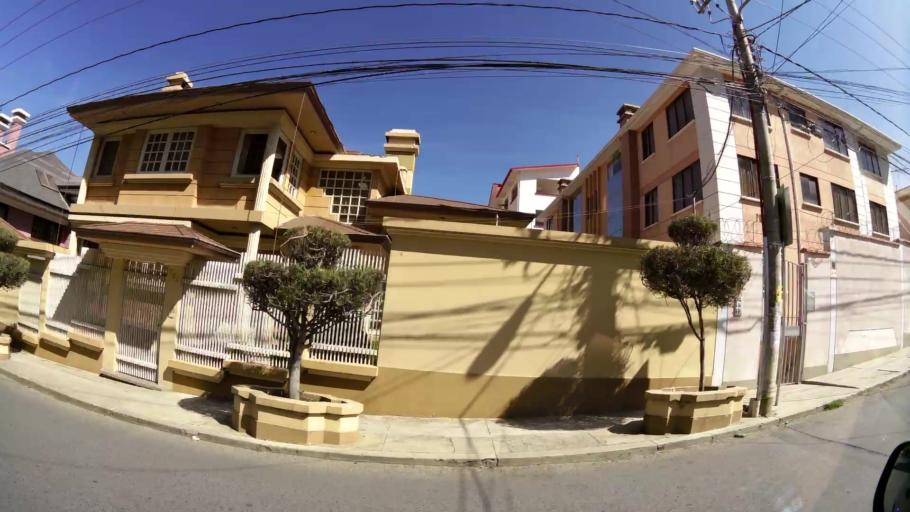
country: BO
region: La Paz
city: La Paz
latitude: -16.5131
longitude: -68.0861
